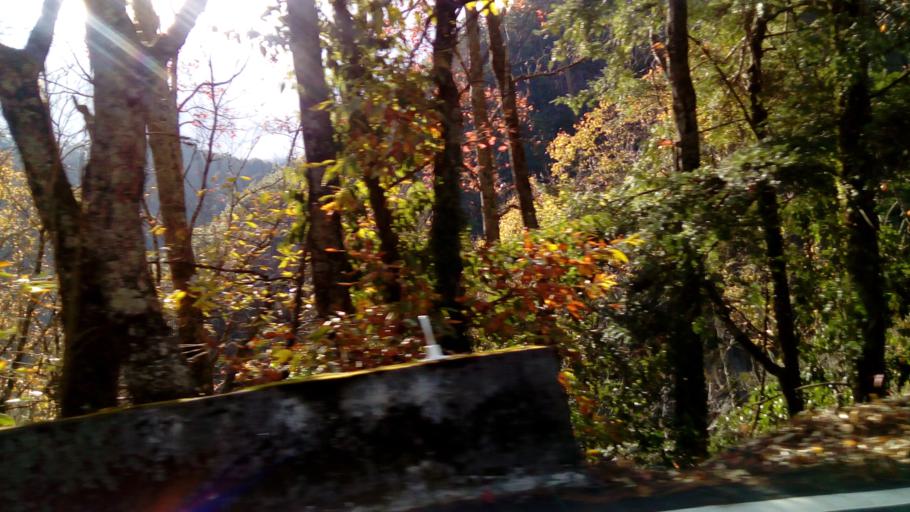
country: TW
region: Taiwan
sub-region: Hualien
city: Hualian
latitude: 24.3466
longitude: 121.3156
